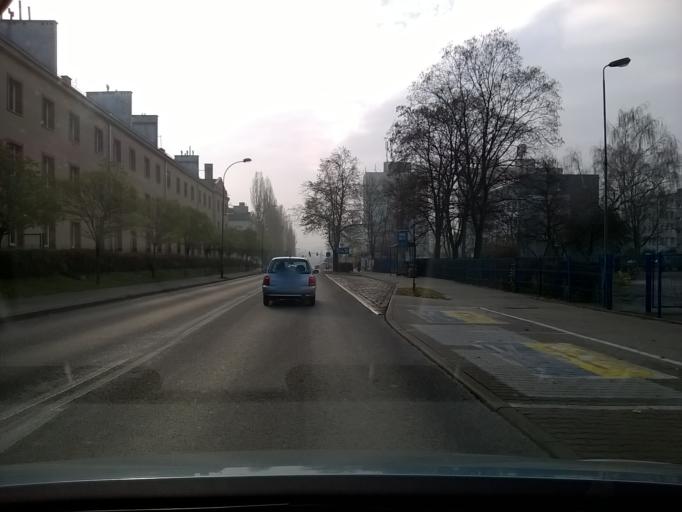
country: PL
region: Silesian Voivodeship
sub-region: Swietochlowice
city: Swietochlowice
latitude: 50.2685
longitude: 18.9375
